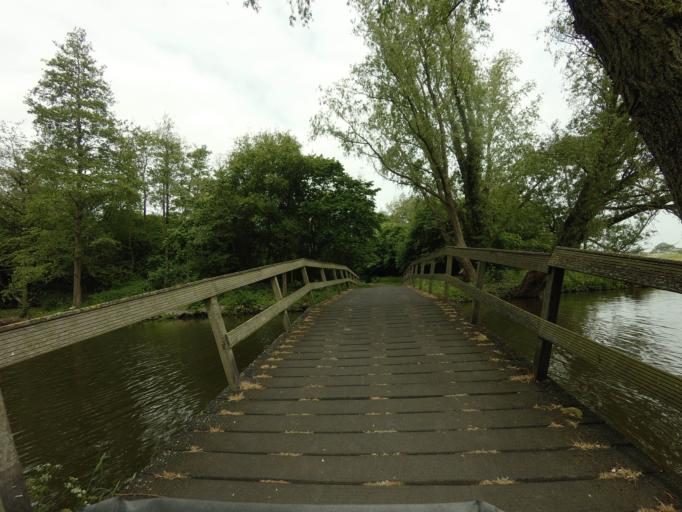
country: NL
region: North Holland
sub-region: Gemeente Medemblik
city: Medemblik
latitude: 52.7397
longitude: 5.1291
